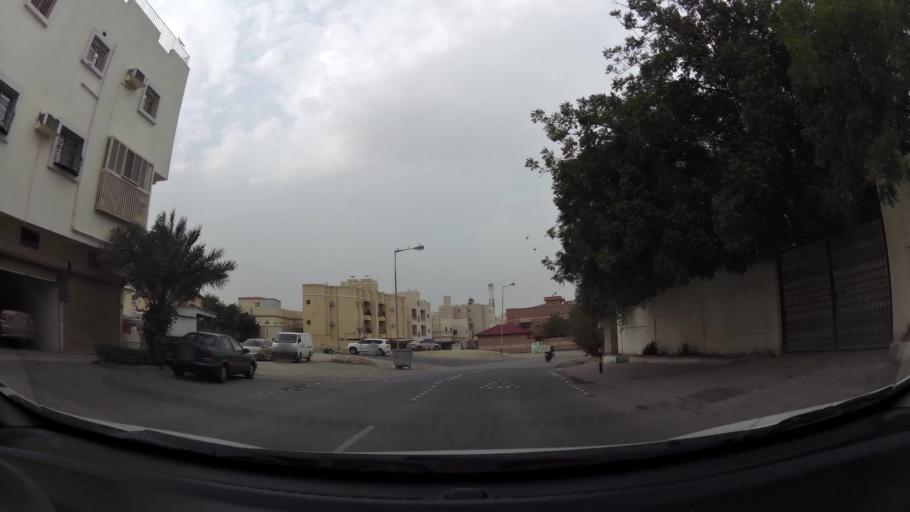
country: BH
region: Northern
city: Ar Rifa'
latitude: 26.1284
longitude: 50.5785
